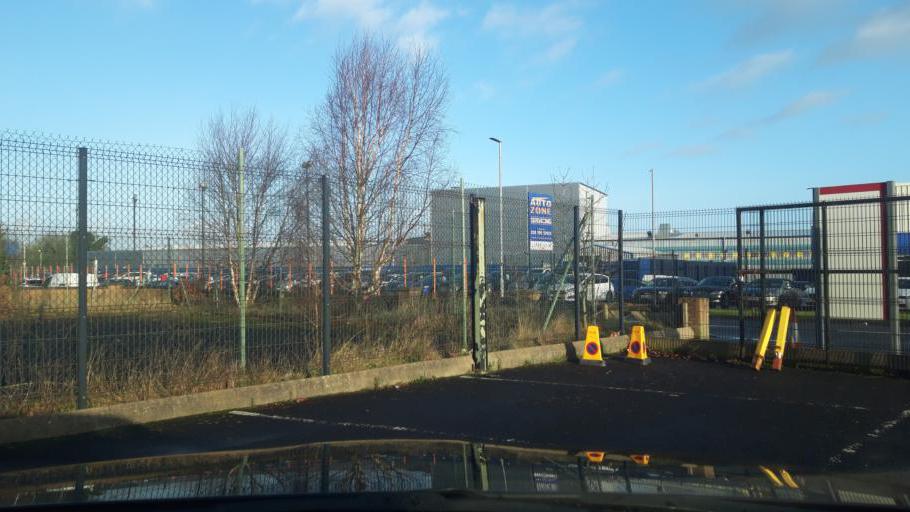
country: GB
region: Northern Ireland
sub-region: Coleraine District
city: Coleraine
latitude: 55.1188
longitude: -6.6793
